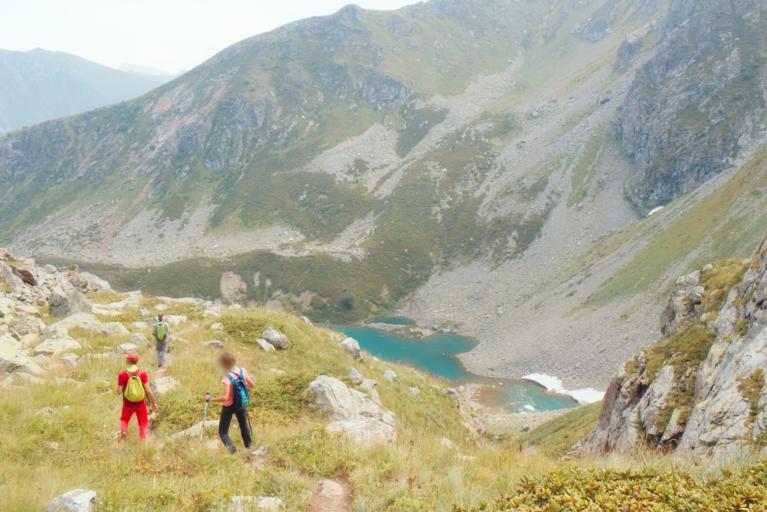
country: RU
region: Karachayevo-Cherkesiya
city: Nizhniy Arkhyz
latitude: 43.4569
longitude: 41.2379
